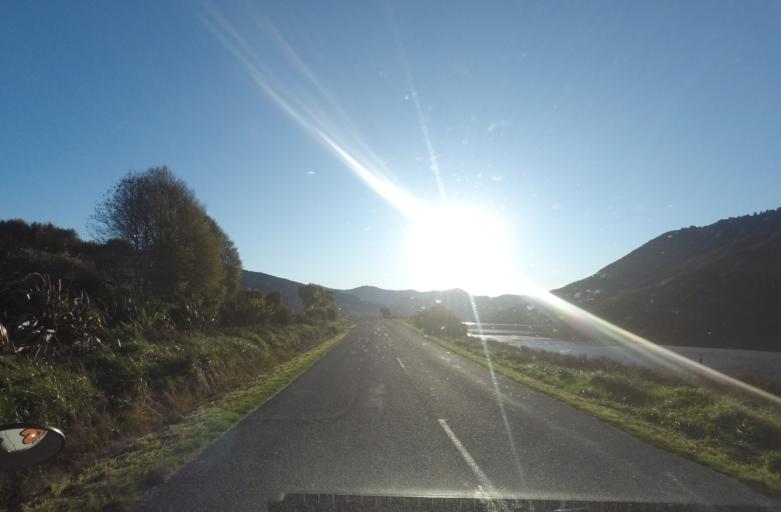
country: NZ
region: Marlborough
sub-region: Marlborough District
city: Picton
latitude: -41.2927
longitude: 173.8319
